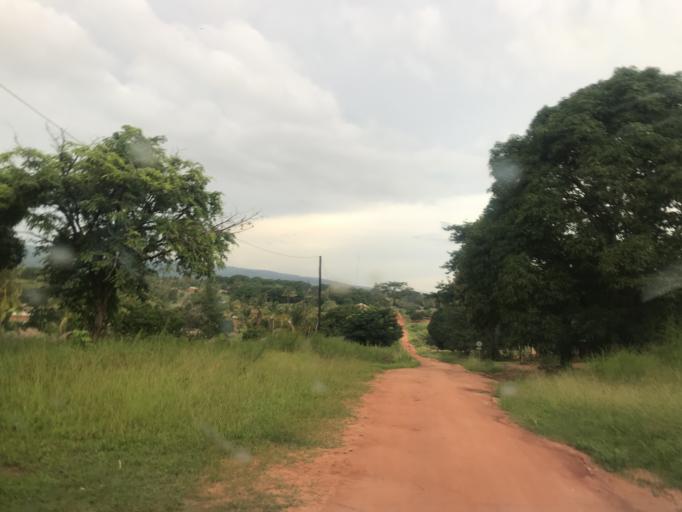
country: TZ
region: Mtwara
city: Newala Kisimani
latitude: -11.3020
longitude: 39.3043
